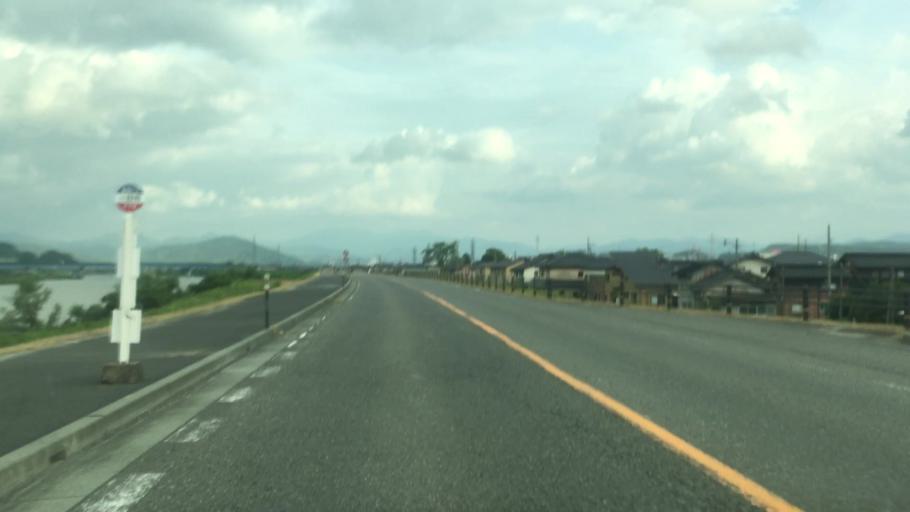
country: JP
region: Hyogo
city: Toyooka
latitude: 35.5629
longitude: 134.8129
